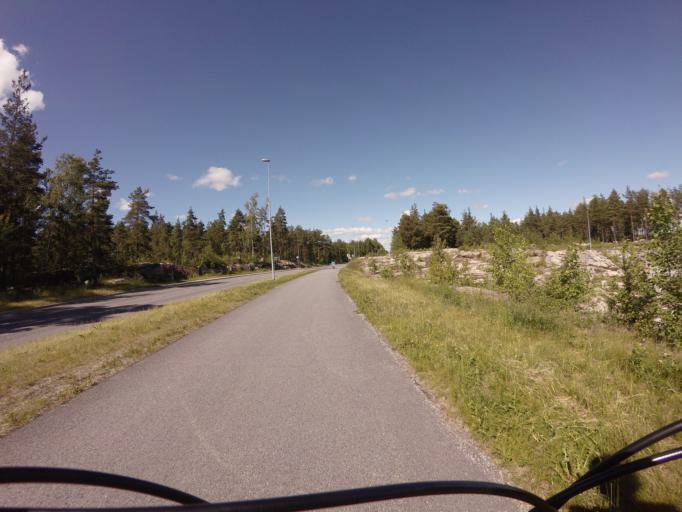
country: FI
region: Varsinais-Suomi
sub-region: Turku
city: Turku
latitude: 60.5031
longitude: 22.2818
